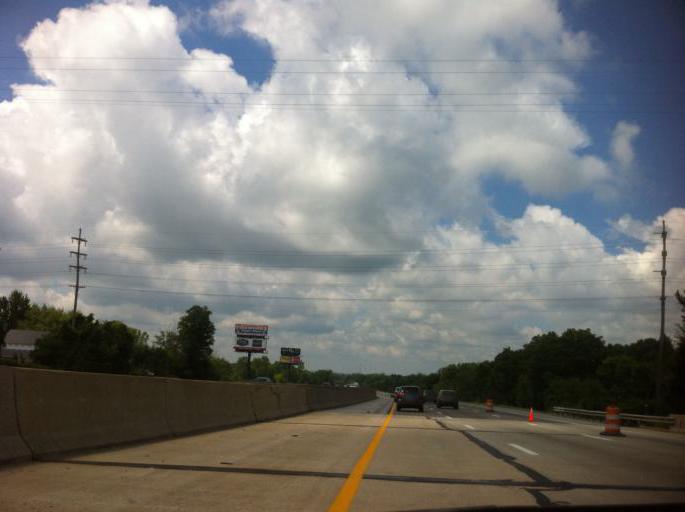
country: US
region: Ohio
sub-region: Erie County
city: Huron
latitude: 41.3289
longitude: -82.4932
